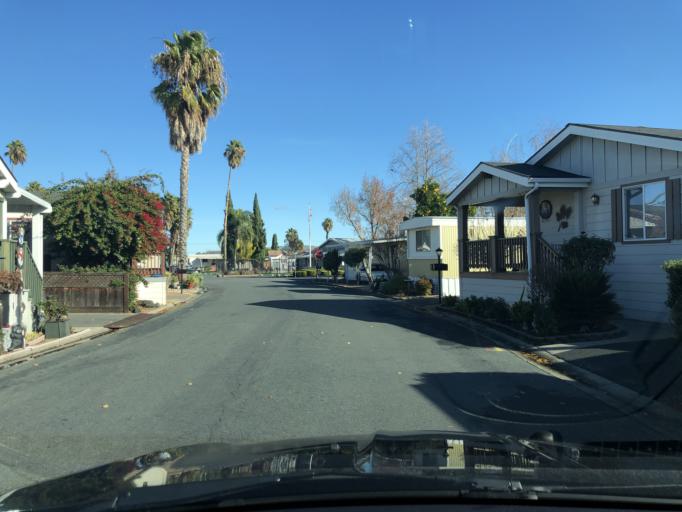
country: US
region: California
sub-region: Contra Costa County
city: Pacheco
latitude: 37.9907
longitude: -122.0660
